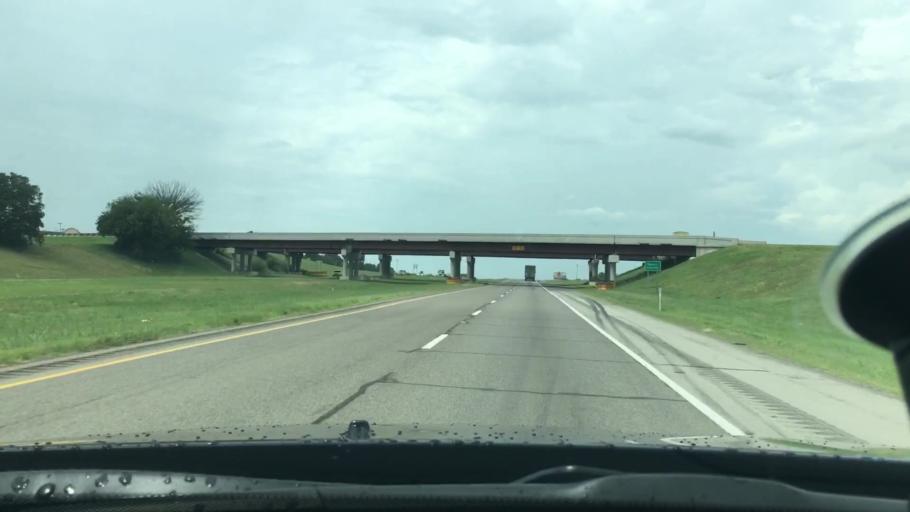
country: US
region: Oklahoma
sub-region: Murray County
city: Davis
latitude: 34.5053
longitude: -97.1732
